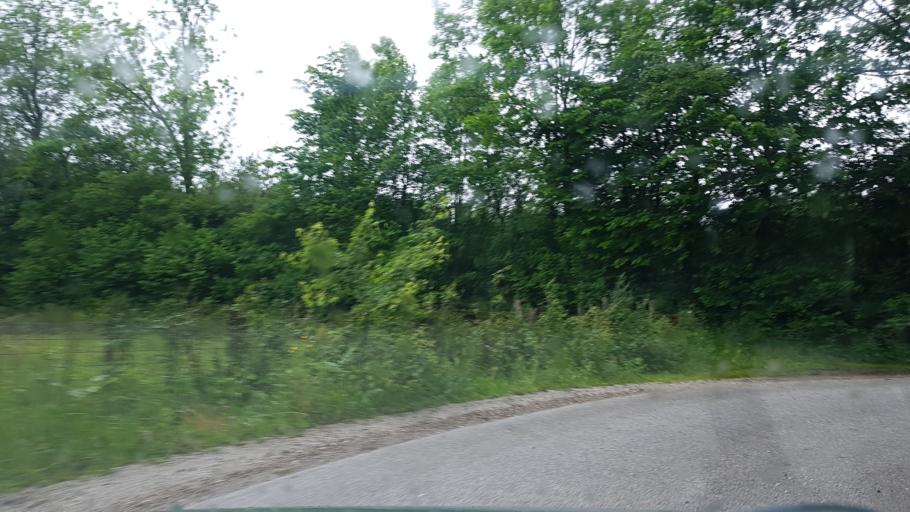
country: SI
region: Bled
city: Zasip
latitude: 46.3862
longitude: 14.1164
